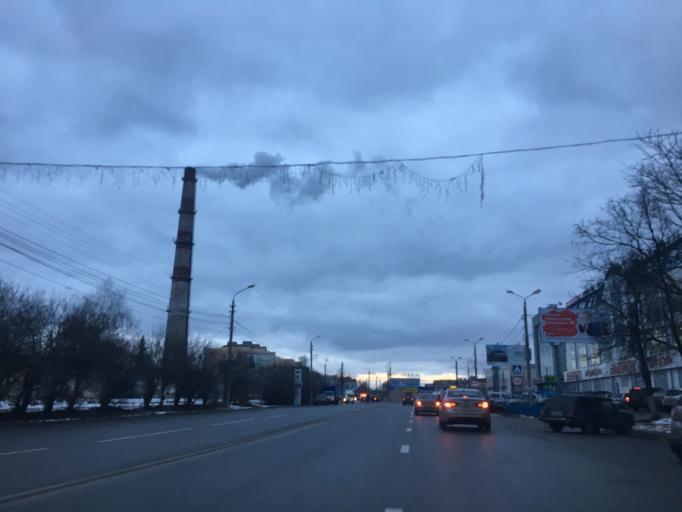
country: RU
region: Tula
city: Tula
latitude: 54.1999
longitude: 37.5913
